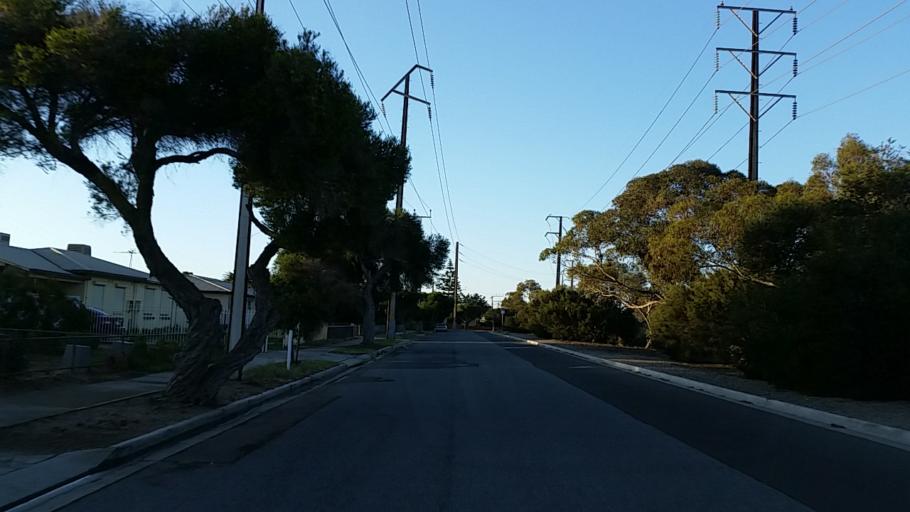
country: AU
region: South Australia
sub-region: Port Adelaide Enfield
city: Birkenhead
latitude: -34.8041
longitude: 138.5056
